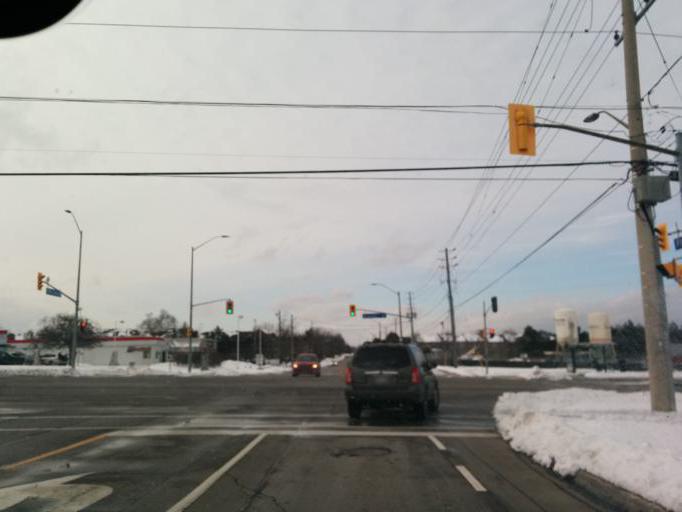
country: CA
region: Ontario
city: Mississauga
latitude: 43.5354
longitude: -79.6673
